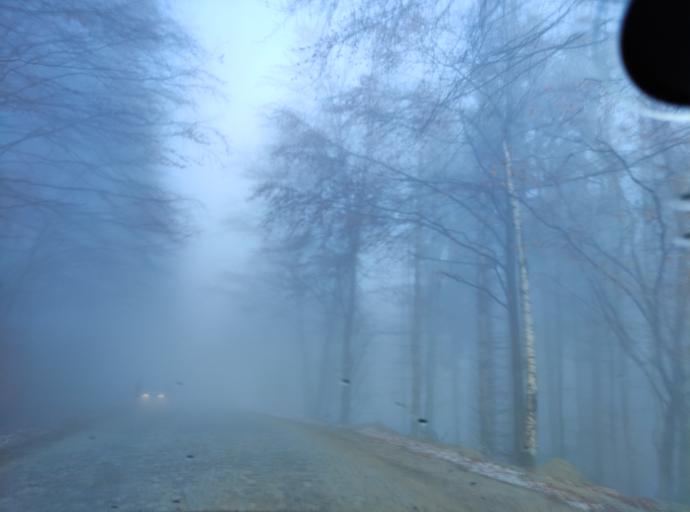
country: BG
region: Sofia-Capital
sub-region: Stolichna Obshtina
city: Sofia
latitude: 42.6109
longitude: 23.2969
